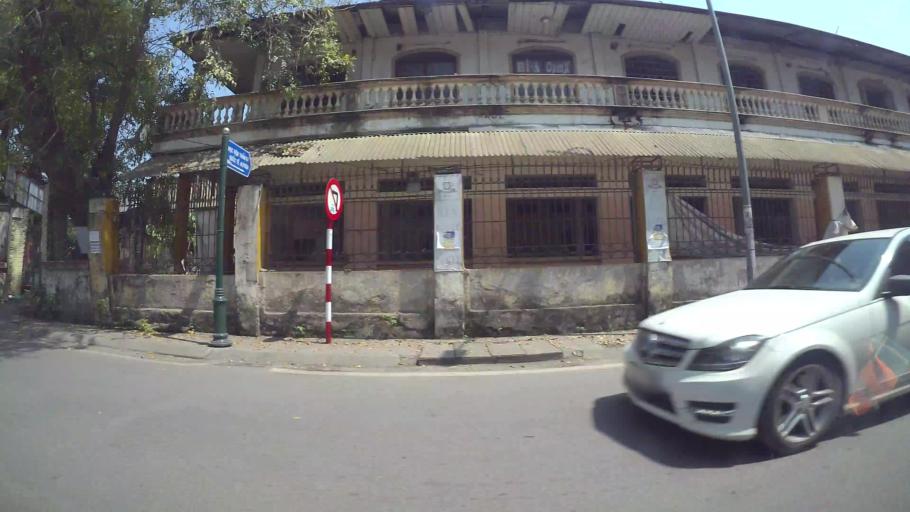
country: VN
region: Ha Noi
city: Hoan Kiem
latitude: 21.0498
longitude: 105.8778
